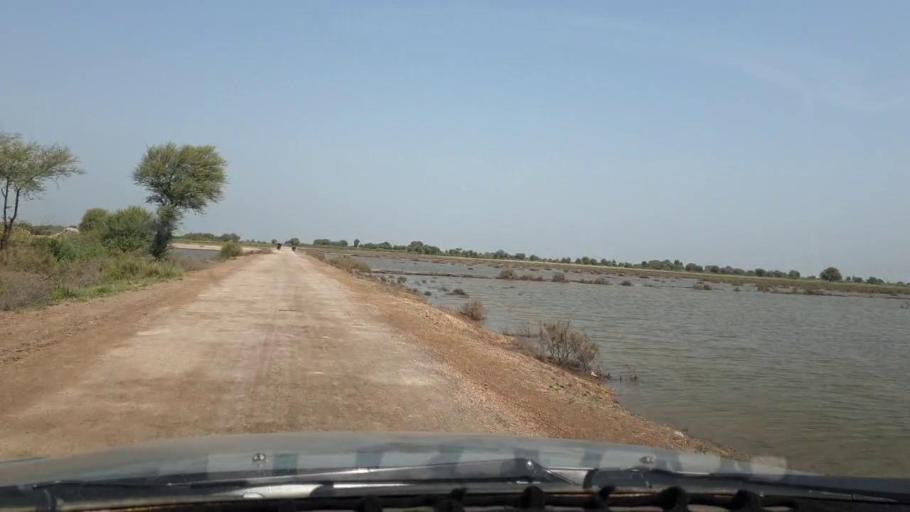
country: PK
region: Sindh
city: Tando Muhammad Khan
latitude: 25.1425
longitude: 68.6324
